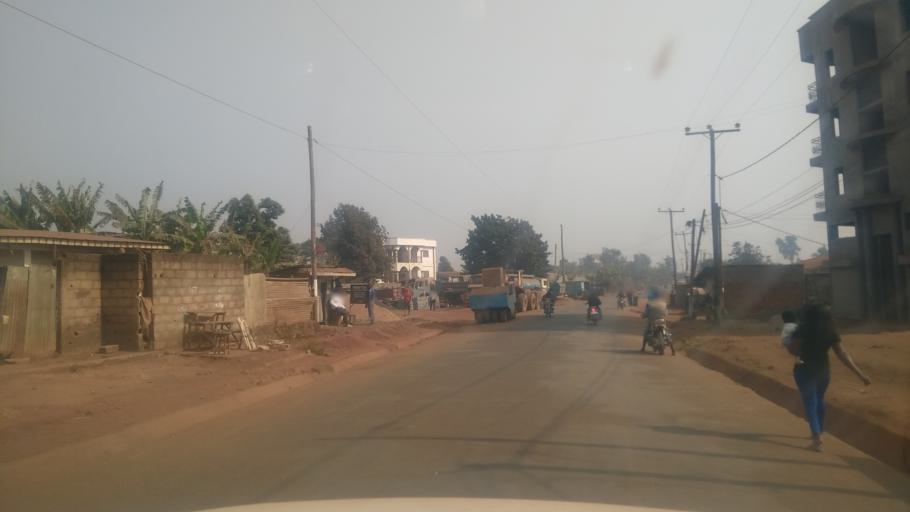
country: CM
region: West
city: Bafoussam
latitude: 5.4993
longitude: 10.3967
